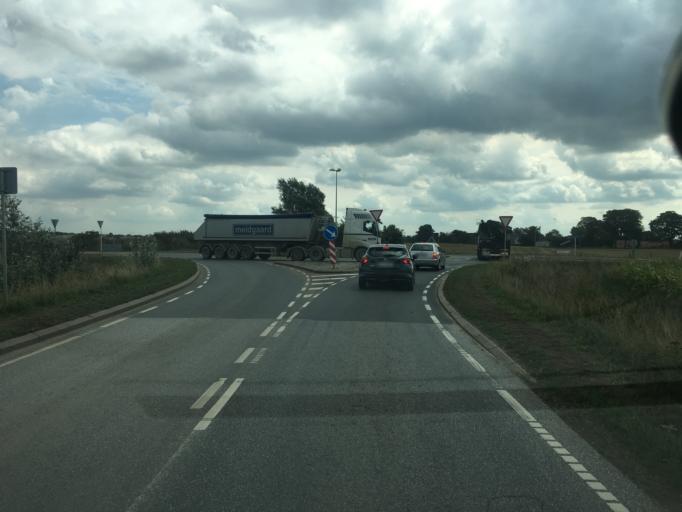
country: DK
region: South Denmark
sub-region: Aabenraa Kommune
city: Tinglev
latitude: 54.9711
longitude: 9.3103
